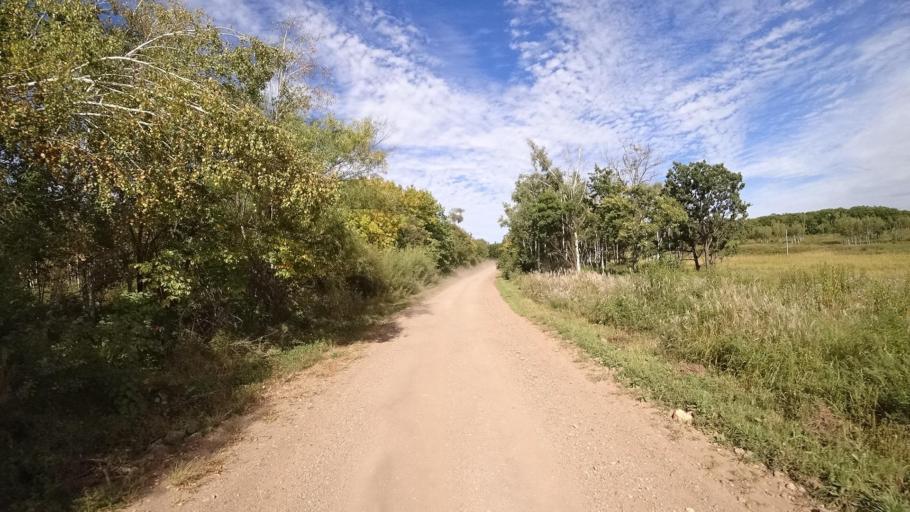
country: RU
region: Primorskiy
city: Yakovlevka
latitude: 44.3907
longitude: 133.5478
